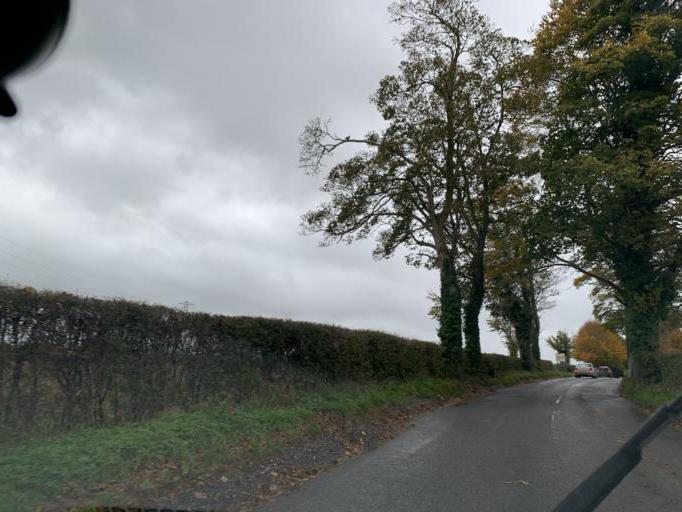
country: GB
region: England
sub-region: Wiltshire
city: Woodford
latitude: 51.1034
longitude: -1.8371
